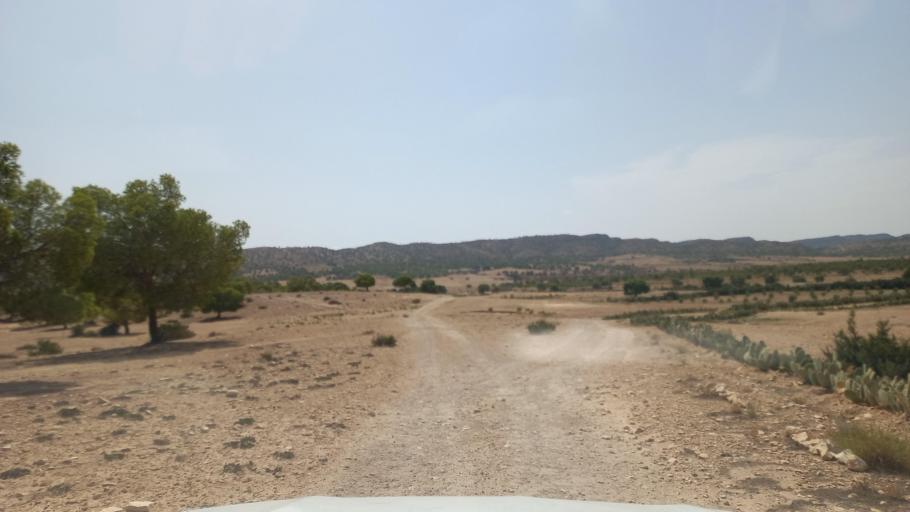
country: TN
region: Al Qasrayn
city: Sbiba
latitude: 35.3969
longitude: 8.9860
